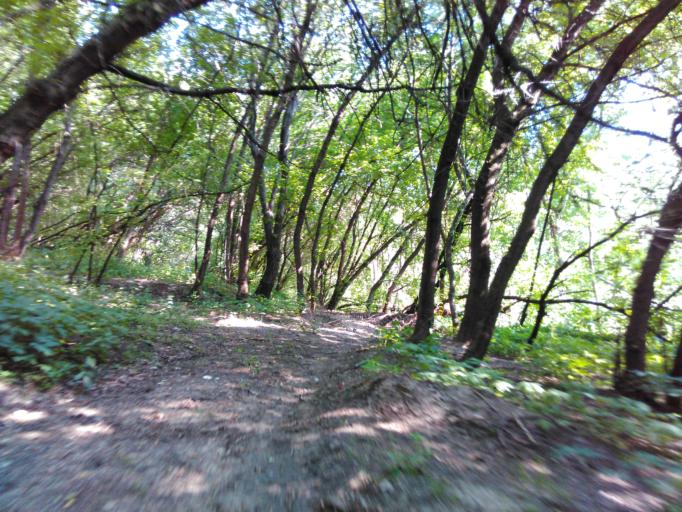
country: RU
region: Moscow
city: Amin'yevo
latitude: 55.7136
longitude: 37.4511
